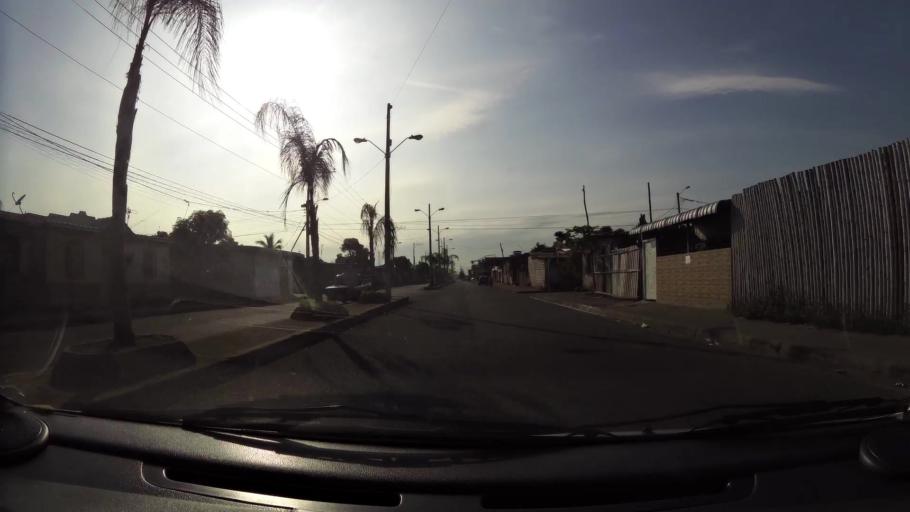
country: EC
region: Guayas
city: Eloy Alfaro
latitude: -2.1824
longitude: -79.8513
